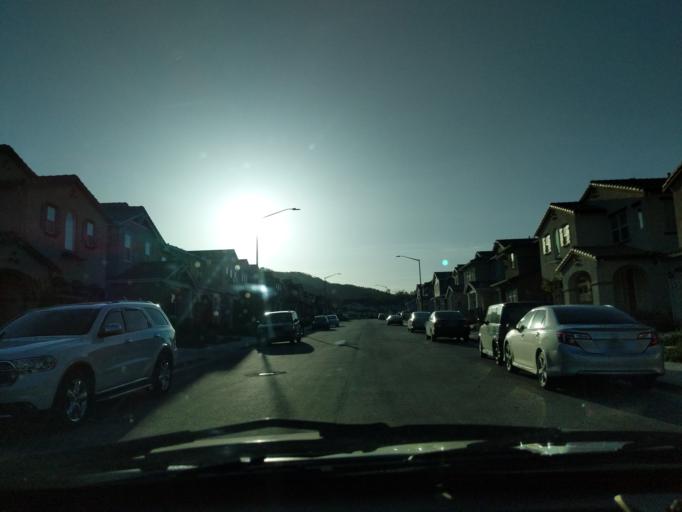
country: US
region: California
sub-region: Santa Clara County
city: Gilroy
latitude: 36.9873
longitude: -121.5807
